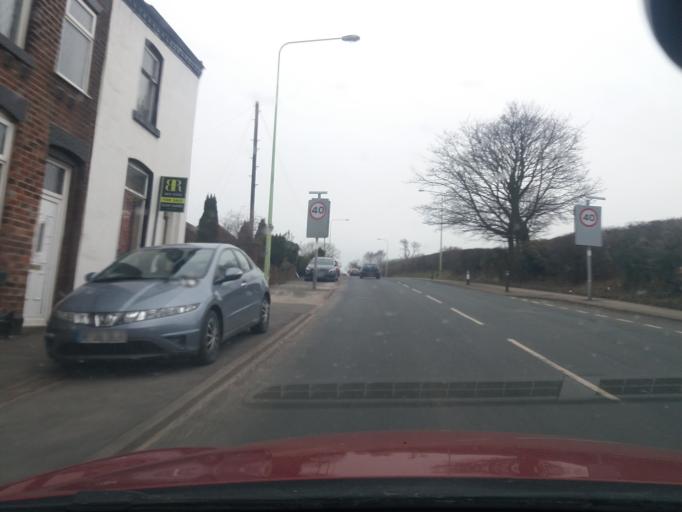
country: GB
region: England
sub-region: Lancashire
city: Chorley
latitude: 53.6658
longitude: -2.6159
